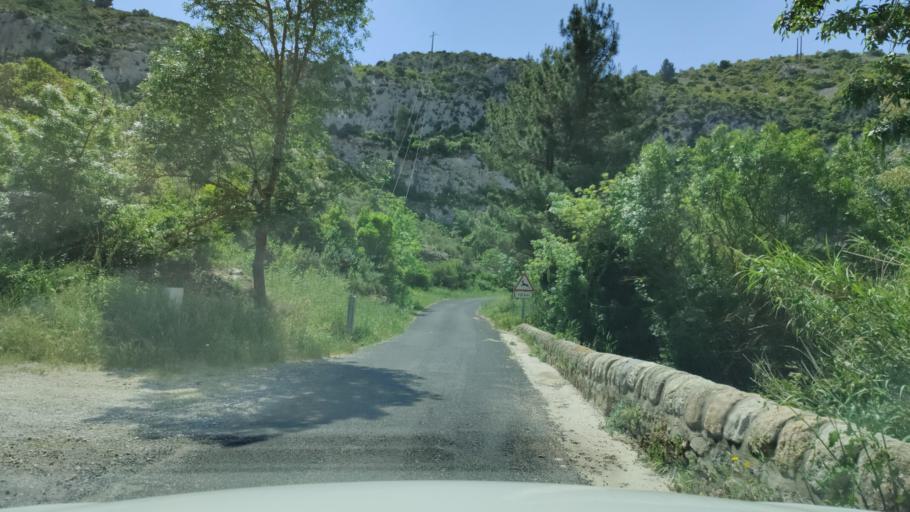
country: FR
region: Languedoc-Roussillon
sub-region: Departement des Pyrenees-Orientales
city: Estagel
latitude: 42.8087
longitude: 2.7449
